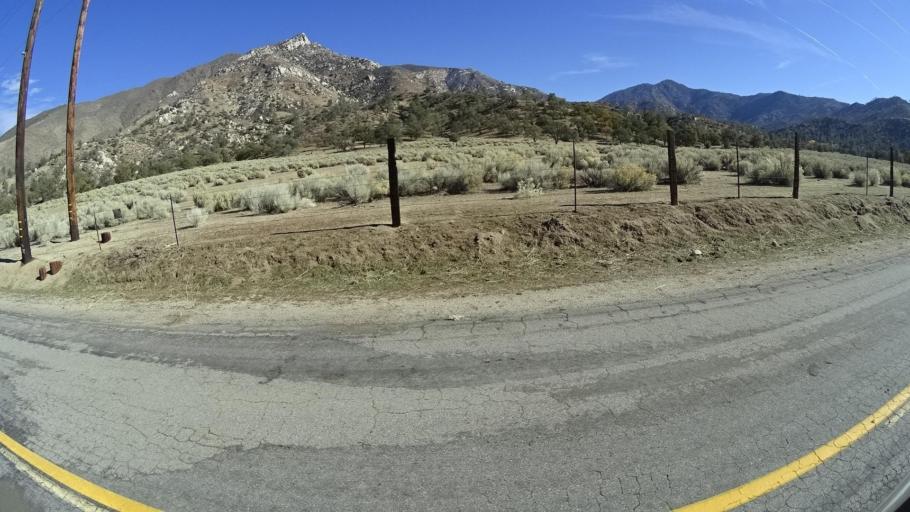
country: US
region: California
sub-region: Kern County
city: Bodfish
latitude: 35.5410
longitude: -118.5099
